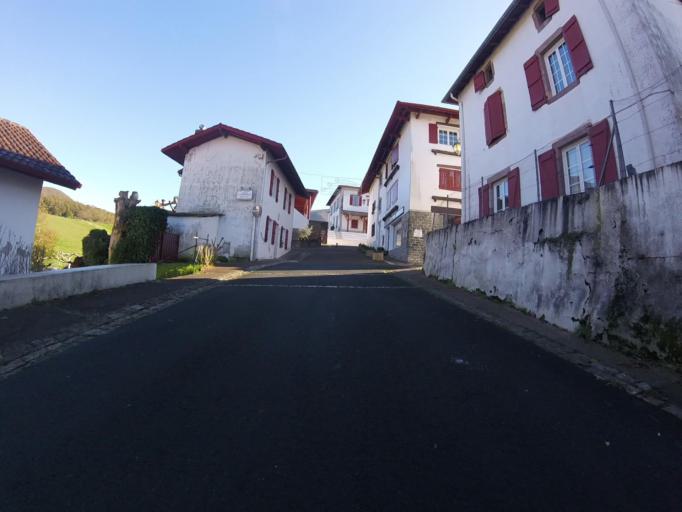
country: ES
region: Basque Country
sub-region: Provincia de Guipuzcoa
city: Irun
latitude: 43.3334
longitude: -1.7435
